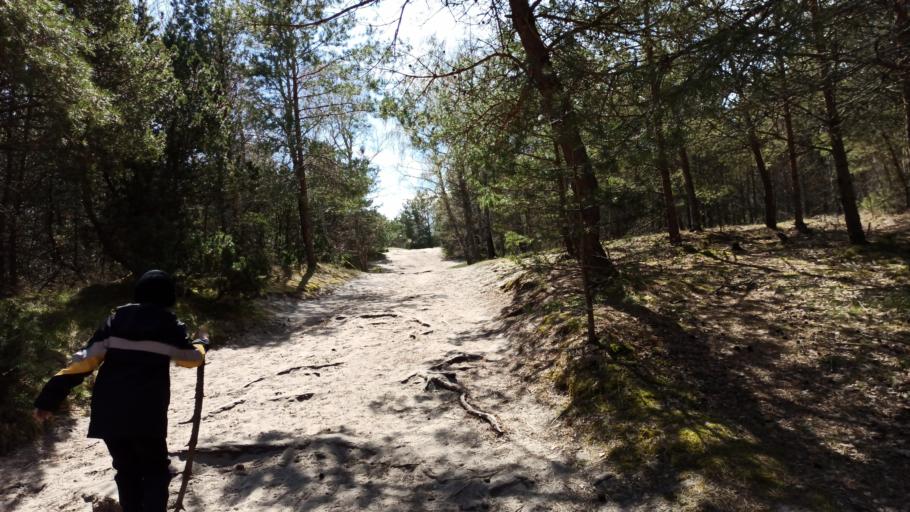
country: LT
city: Nida
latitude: 55.1491
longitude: 20.8124
